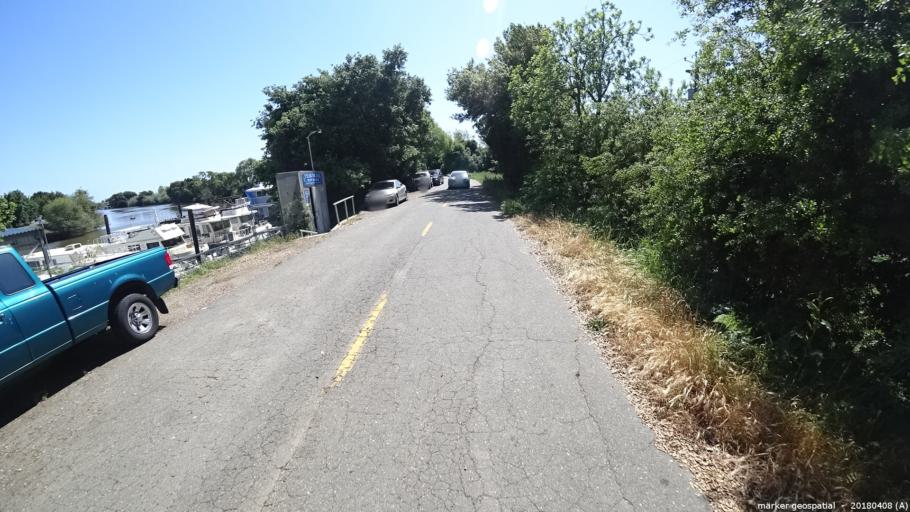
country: US
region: California
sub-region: Sacramento County
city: Walnut Grove
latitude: 38.2292
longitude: -121.5117
